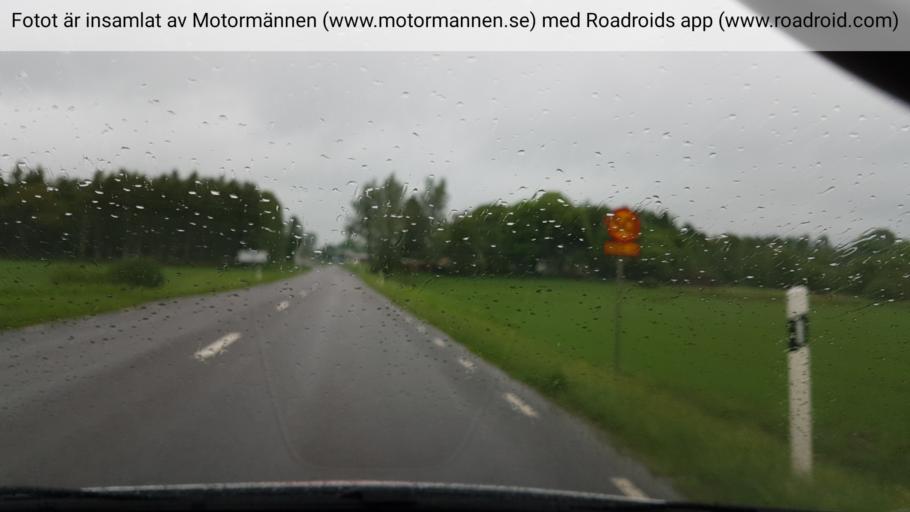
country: SE
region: Vaestra Goetaland
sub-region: Falkopings Kommun
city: Falkoeping
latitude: 58.0674
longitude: 13.5275
